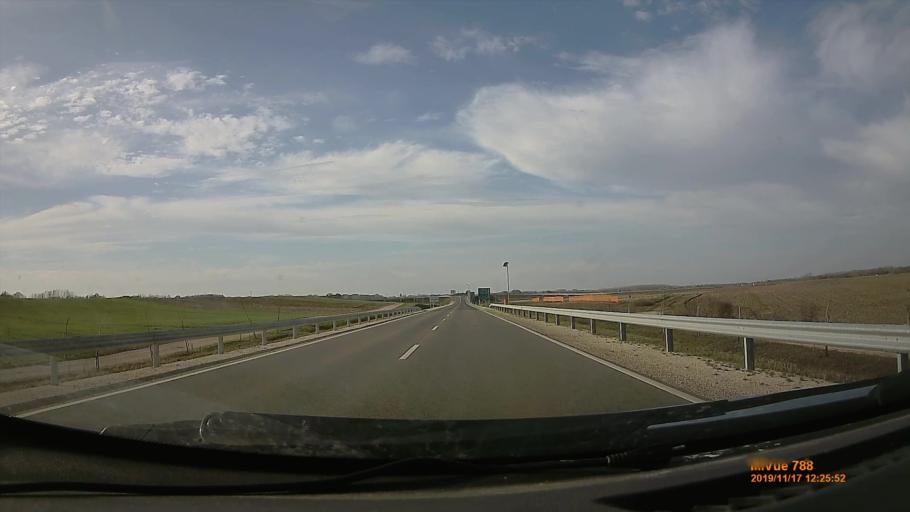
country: HU
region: Bacs-Kiskun
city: Kecskemet
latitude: 46.9316
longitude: 19.6266
